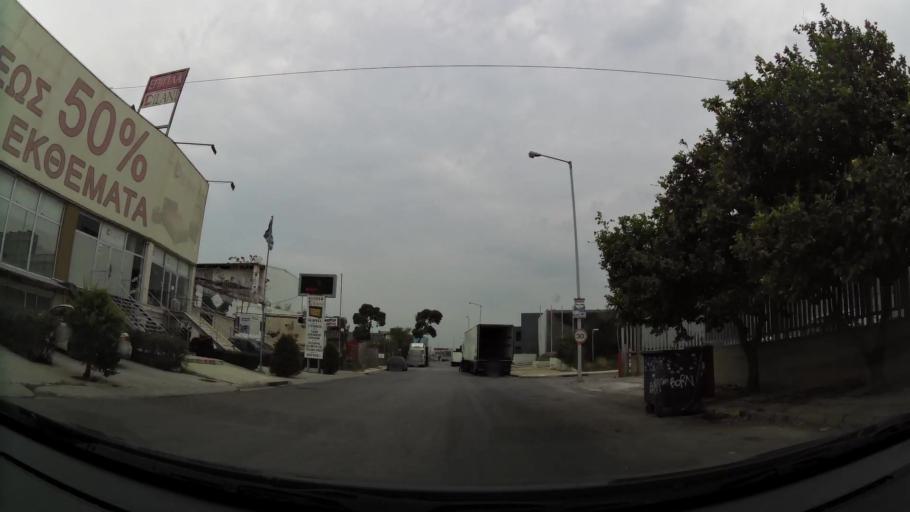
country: GR
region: Attica
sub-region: Nomarchia Athinas
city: Aigaleo
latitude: 37.9729
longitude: 23.6771
